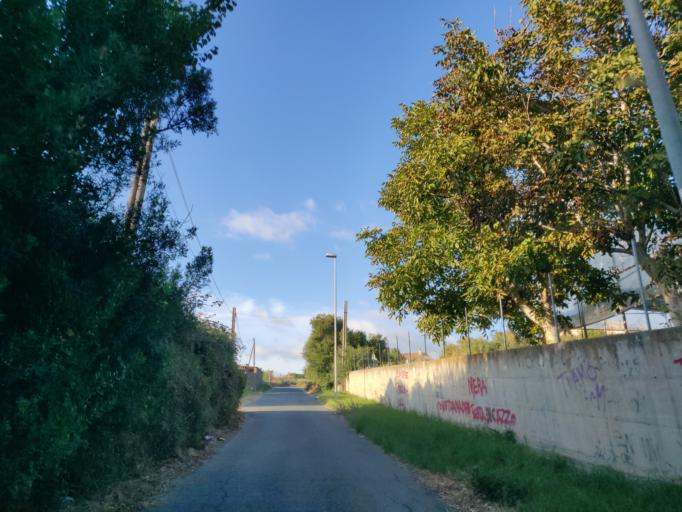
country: IT
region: Latium
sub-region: Citta metropolitana di Roma Capitale
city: Civitavecchia
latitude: 42.0930
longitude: 11.8182
